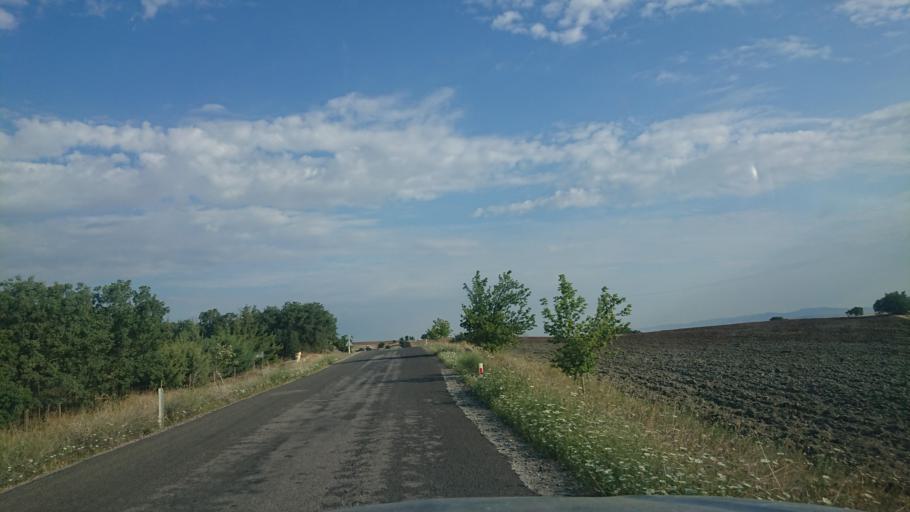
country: TR
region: Aksaray
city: Ortakoy
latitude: 38.8069
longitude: 34.0595
